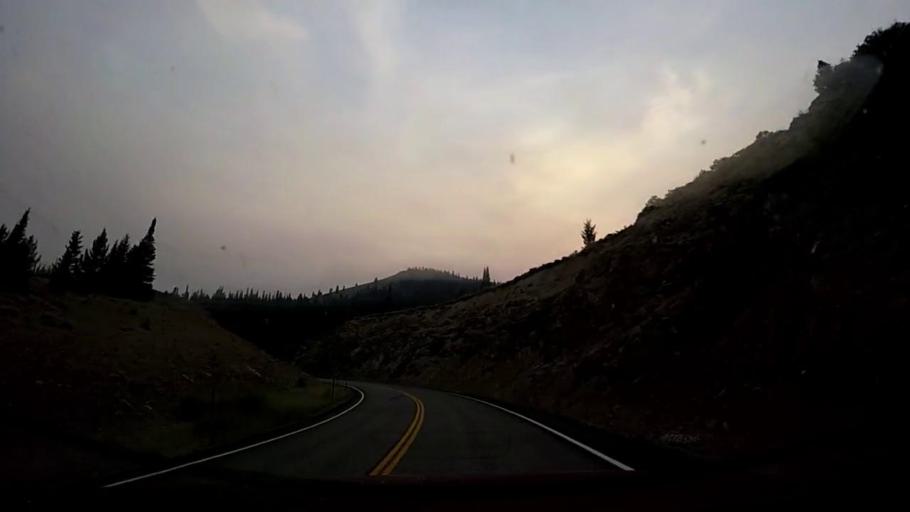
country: US
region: Idaho
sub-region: Blaine County
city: Ketchum
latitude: 43.8825
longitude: -114.7003
